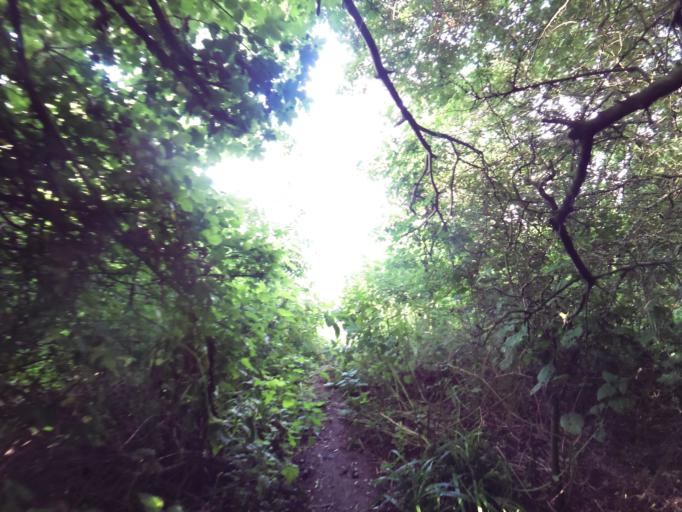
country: GB
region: England
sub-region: Suffolk
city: Ipswich
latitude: 52.0847
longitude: 1.1637
